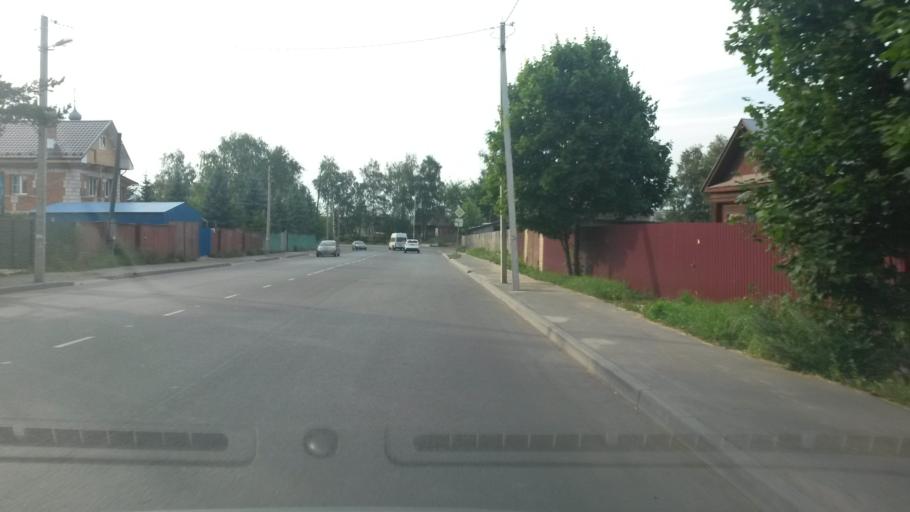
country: RU
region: Ivanovo
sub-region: Gorod Ivanovo
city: Ivanovo
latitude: 57.0191
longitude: 40.9229
